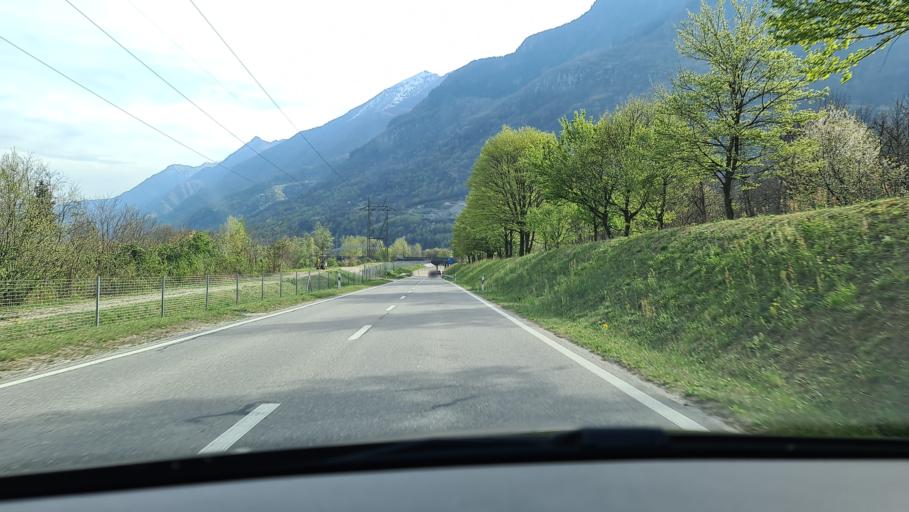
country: CH
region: Ticino
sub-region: Riviera District
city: Biasca
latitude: 46.3638
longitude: 8.9608
